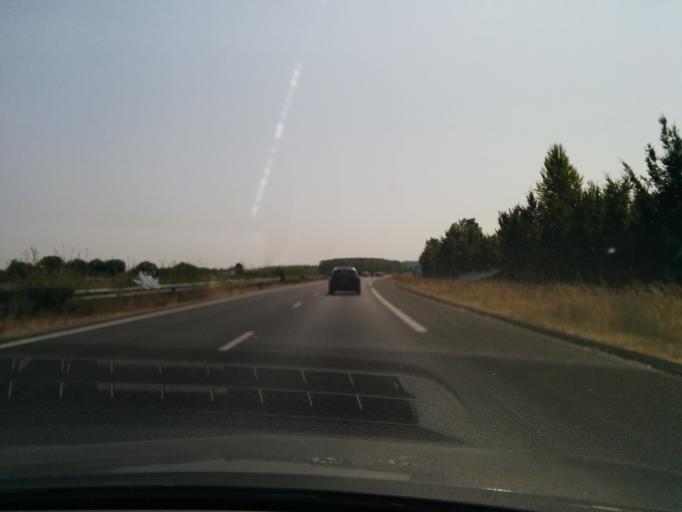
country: FR
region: Midi-Pyrenees
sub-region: Departement du Tarn
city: Lagrave
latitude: 43.8887
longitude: 1.9728
